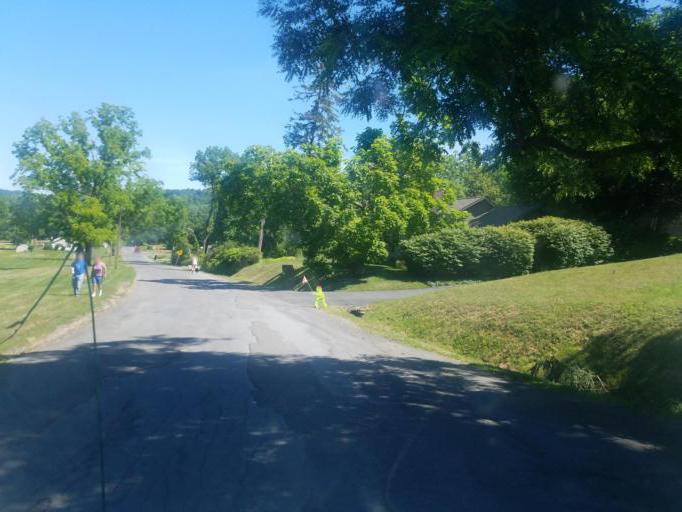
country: US
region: New York
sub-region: Ontario County
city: Naples
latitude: 42.7212
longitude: -77.3244
